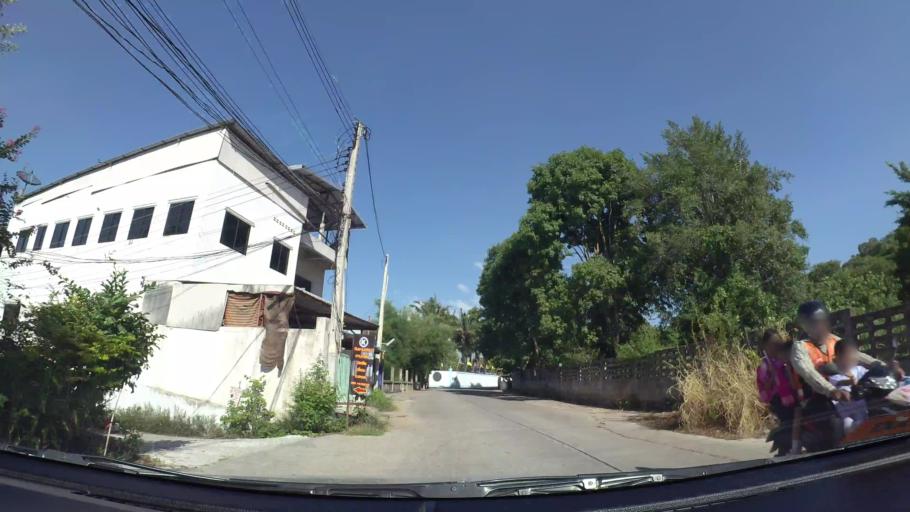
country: TH
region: Chon Buri
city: Si Racha
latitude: 13.1587
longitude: 100.9282
